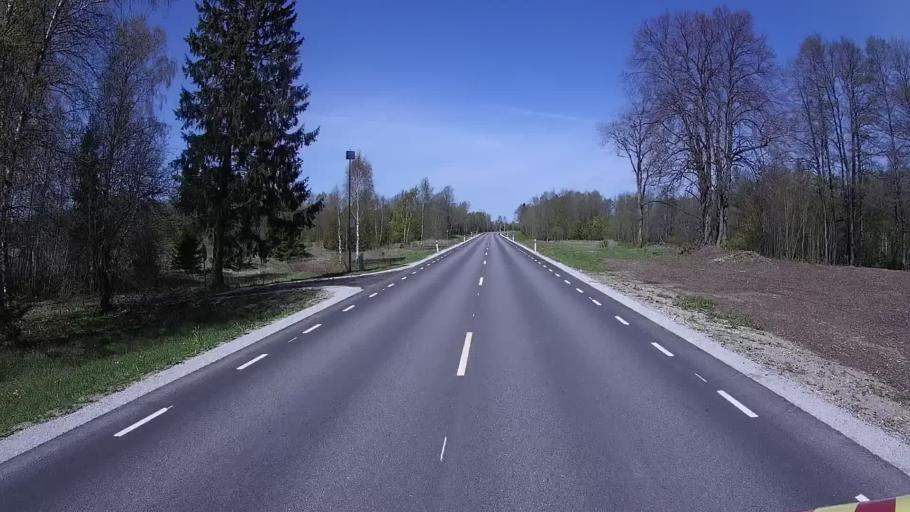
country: EE
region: Harju
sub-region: Nissi vald
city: Turba
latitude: 59.1536
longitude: 24.0758
